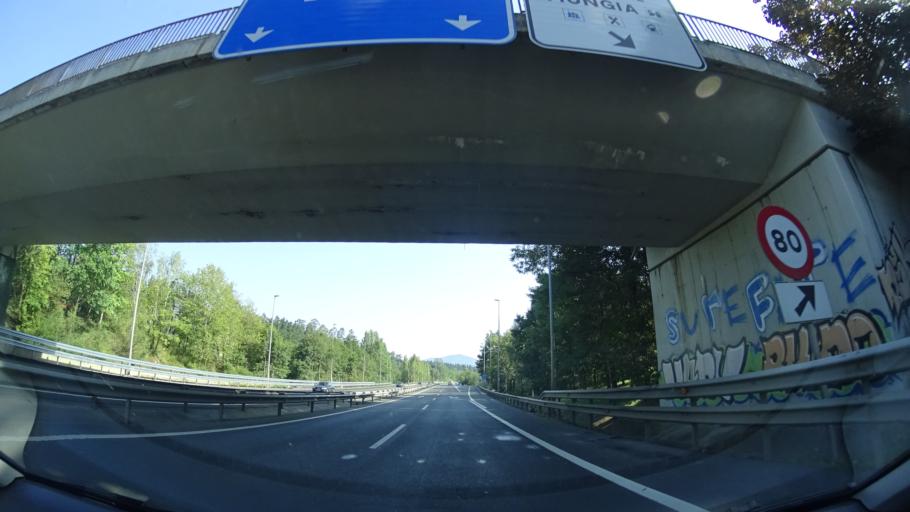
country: ES
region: Basque Country
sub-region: Bizkaia
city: Derio
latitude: 43.3293
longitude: -2.8706
